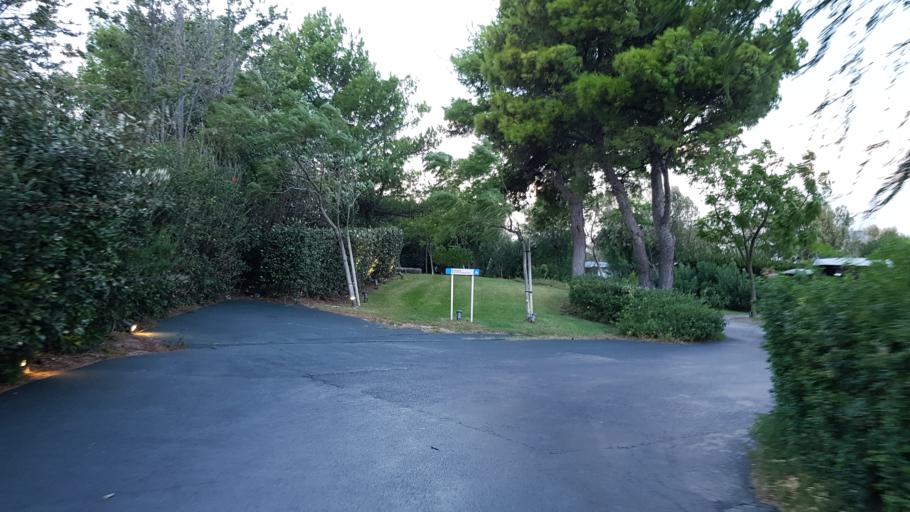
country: GR
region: Attica
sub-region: Nomarchia Anatolikis Attikis
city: Saronida
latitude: 37.7801
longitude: 23.8891
